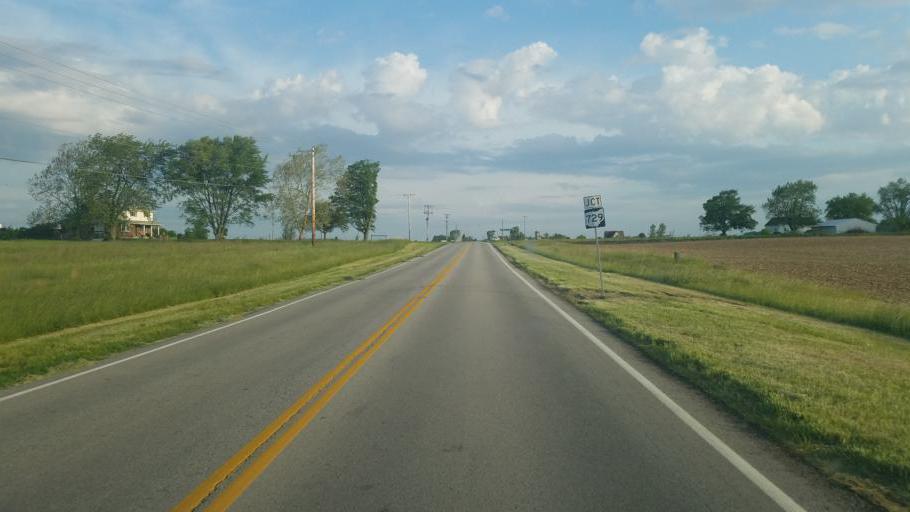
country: US
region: Ohio
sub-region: Clinton County
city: Sabina
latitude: 39.4303
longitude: -83.6284
